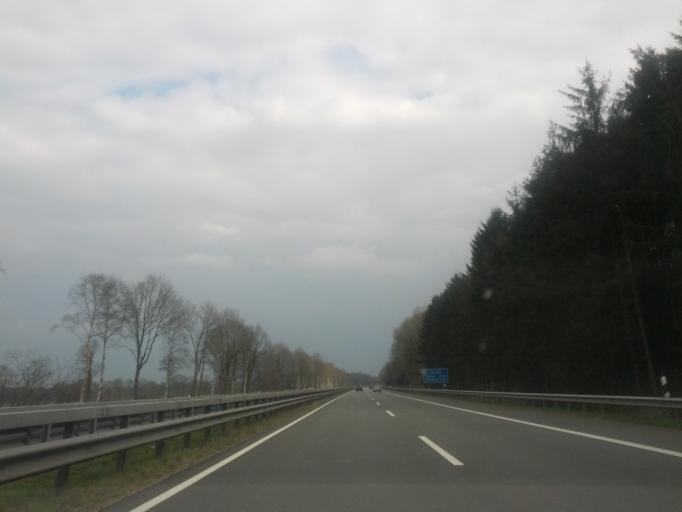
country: DE
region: Lower Saxony
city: Westerstede
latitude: 53.2520
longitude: 7.9759
